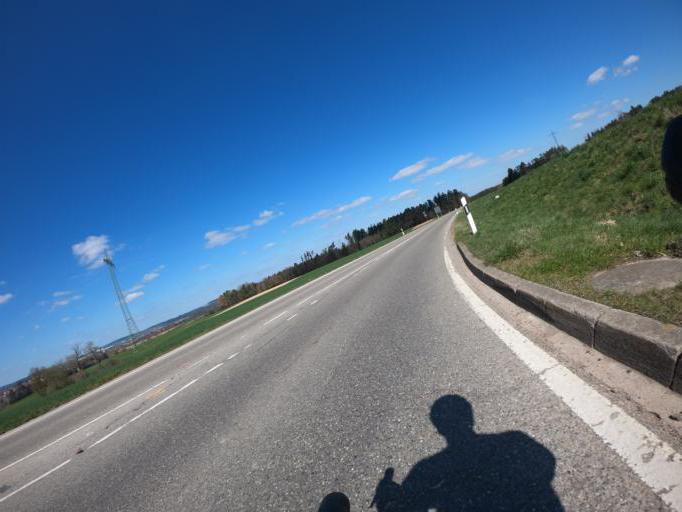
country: DE
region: Baden-Wuerttemberg
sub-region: Karlsruhe Region
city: Horb am Neckar
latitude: 48.4294
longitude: 8.7225
